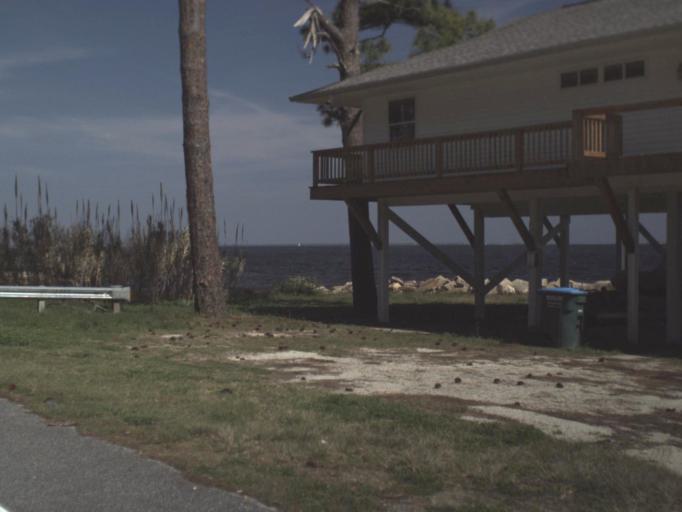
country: US
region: Florida
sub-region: Franklin County
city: Carrabelle
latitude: 29.8150
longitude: -84.7163
